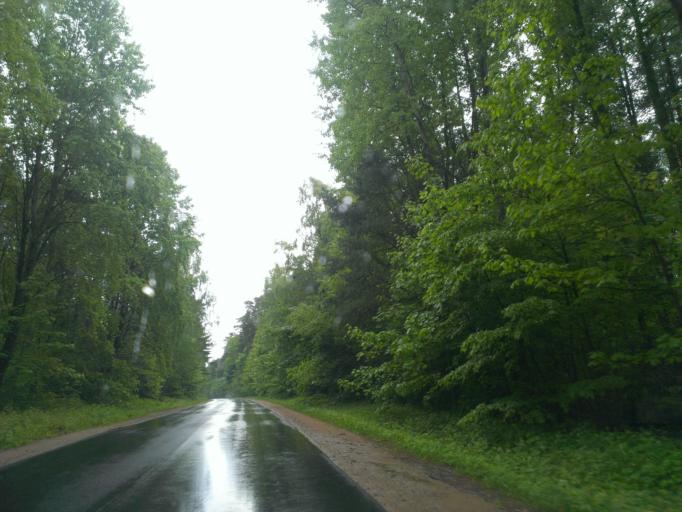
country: LT
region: Klaipedos apskritis
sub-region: Klaipeda
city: Klaipeda
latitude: 55.7864
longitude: 21.0751
